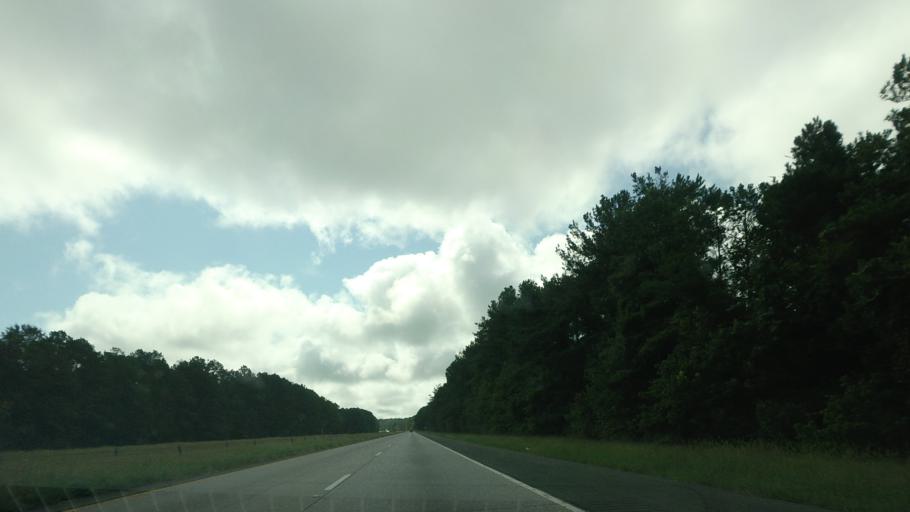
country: US
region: Georgia
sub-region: Twiggs County
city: Jeffersonville
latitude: 32.6438
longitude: -83.4082
